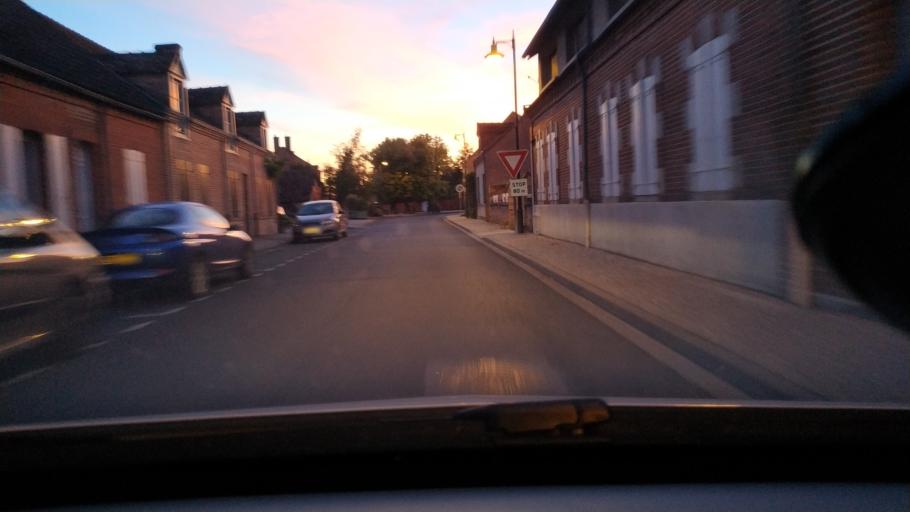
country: FR
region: Centre
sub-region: Departement du Cher
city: Brinon-sur-Sauldre
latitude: 47.6088
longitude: 2.1736
